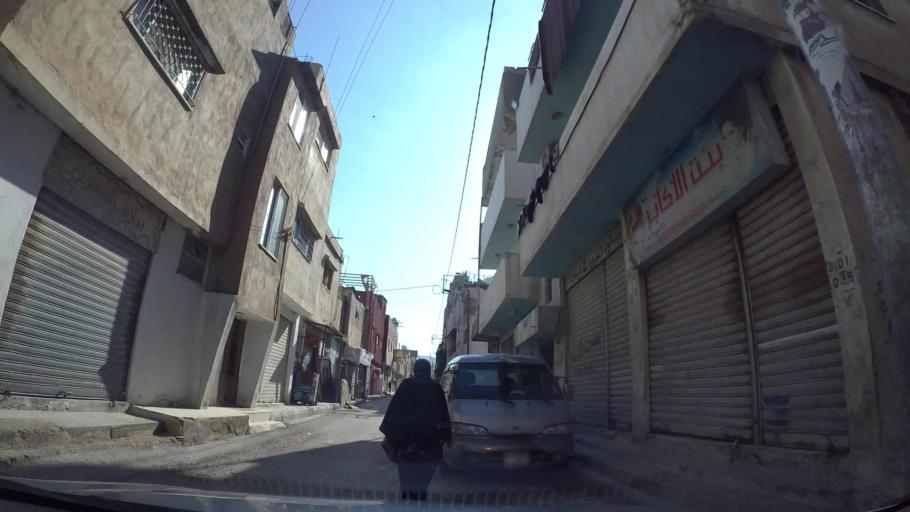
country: JO
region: Amman
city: Al Jubayhah
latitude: 32.0755
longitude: 35.8407
